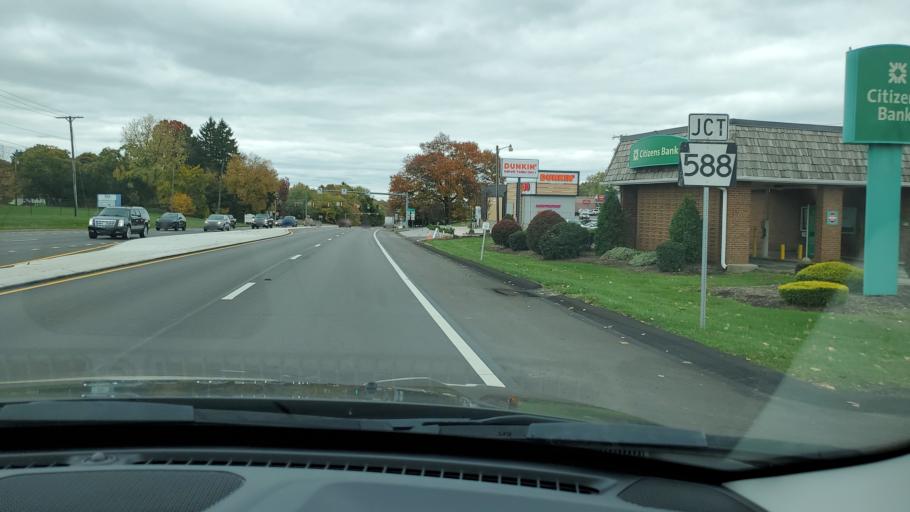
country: US
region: Pennsylvania
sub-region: Beaver County
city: West Mayfield
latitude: 40.7726
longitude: -80.3736
